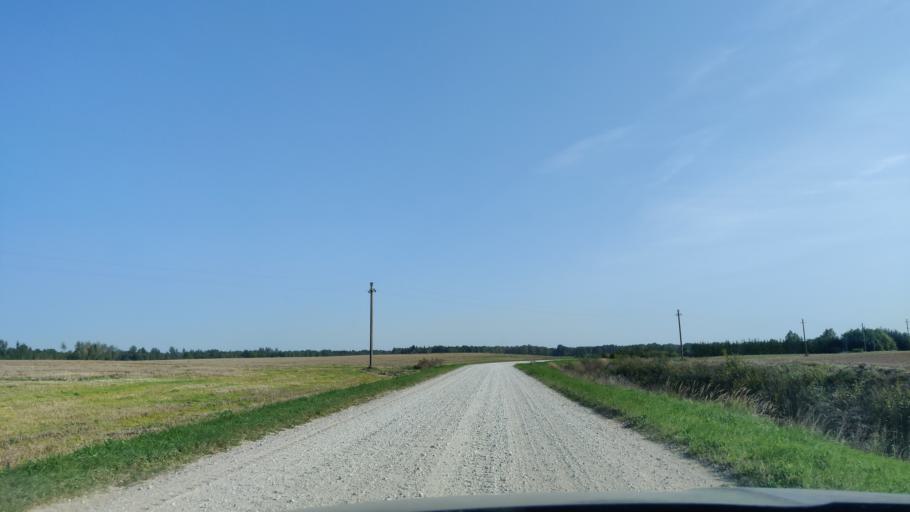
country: LT
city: Sirvintos
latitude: 54.9677
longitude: 24.8459
